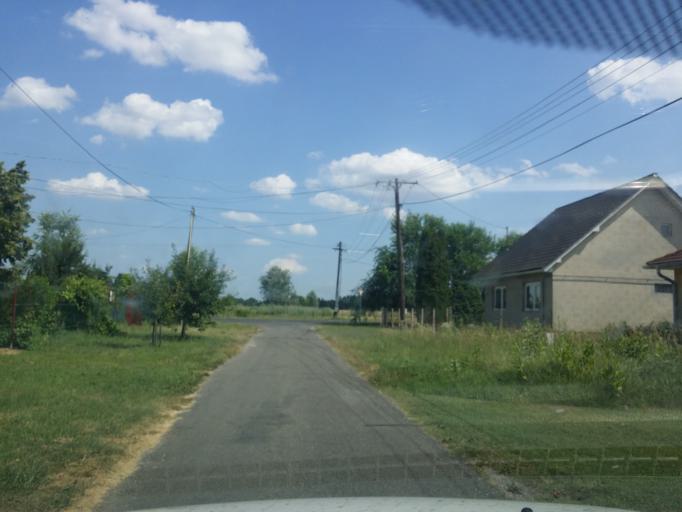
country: HU
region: Bacs-Kiskun
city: Jaszszentlaszlo
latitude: 46.5710
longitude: 19.7656
